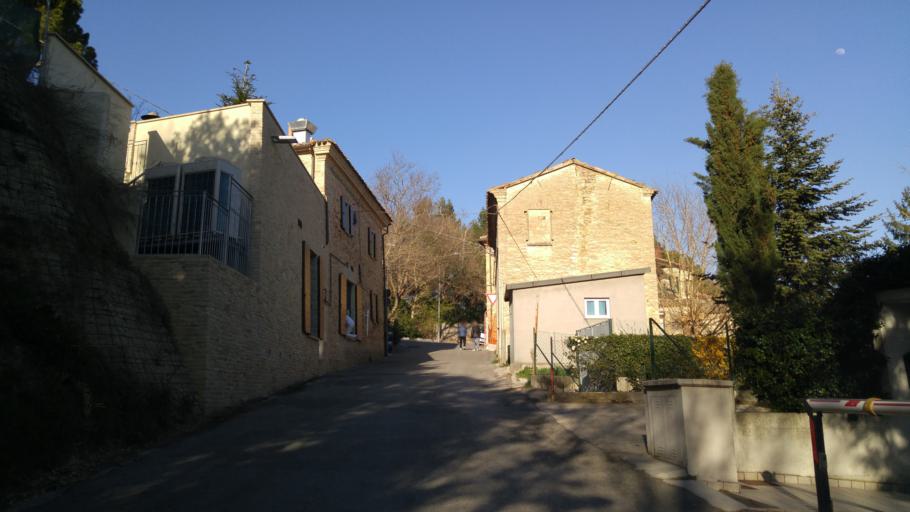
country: IT
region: The Marches
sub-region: Provincia di Pesaro e Urbino
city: Fenile
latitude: 43.8585
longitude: 12.9323
